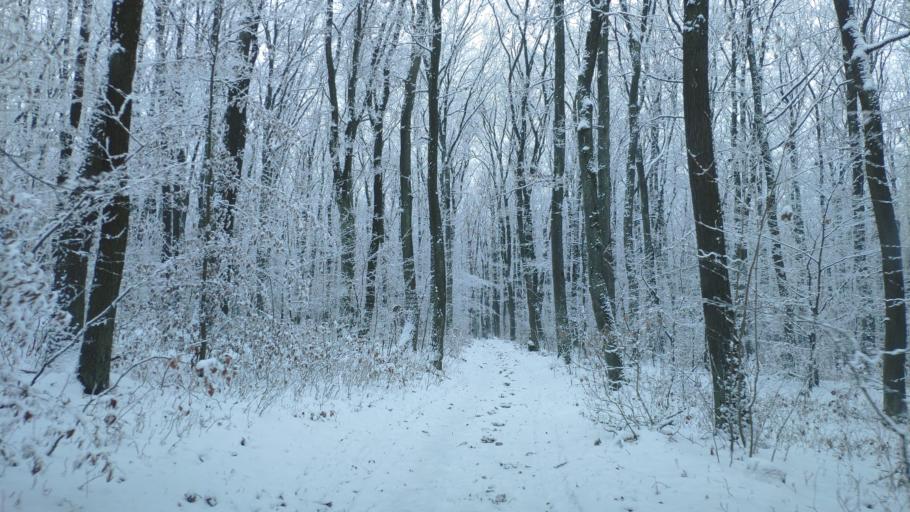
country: SK
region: Kosicky
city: Kosice
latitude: 48.6596
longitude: 21.1832
